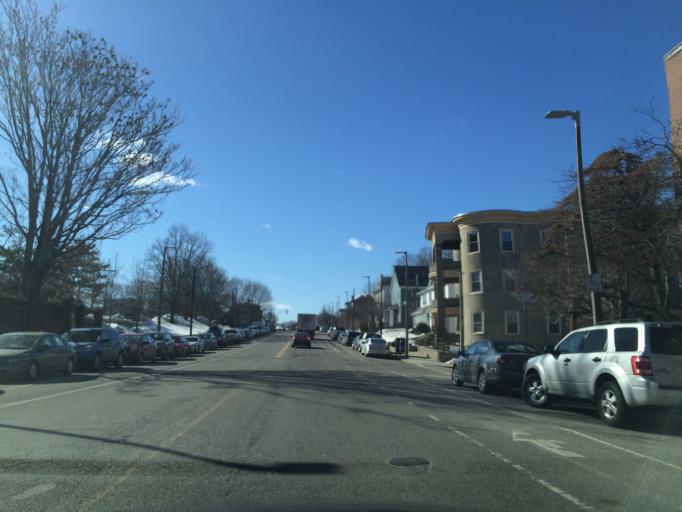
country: US
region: Massachusetts
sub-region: Norfolk County
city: Brookline
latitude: 42.3235
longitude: -71.1122
